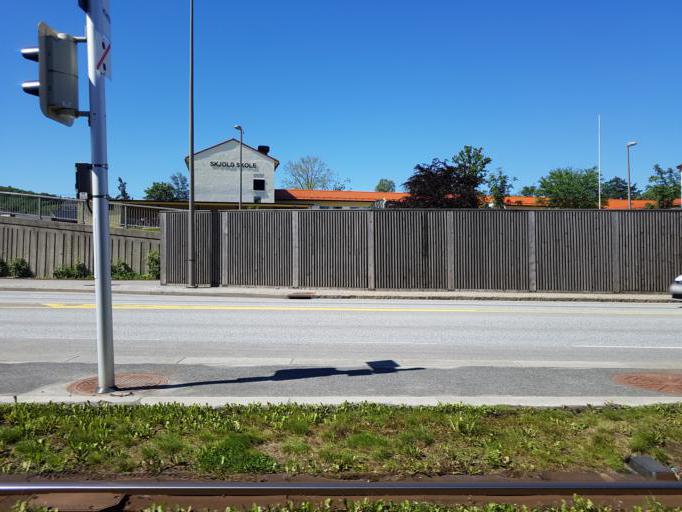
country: NO
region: Hordaland
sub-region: Bergen
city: Sandsli
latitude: 60.3045
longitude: 5.3333
